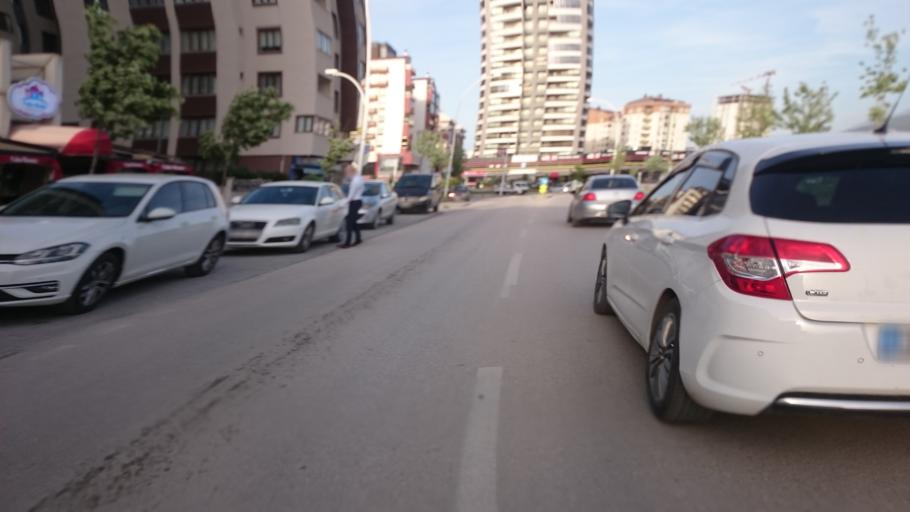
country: TR
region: Bursa
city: Cali
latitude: 40.2165
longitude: 28.9407
